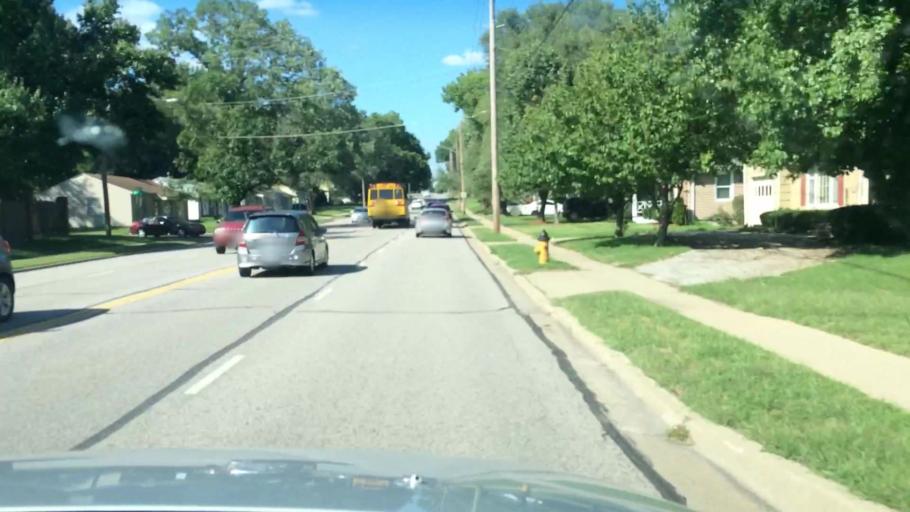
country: US
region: Kansas
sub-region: Johnson County
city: Prairie Village
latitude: 38.9945
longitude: -94.6490
